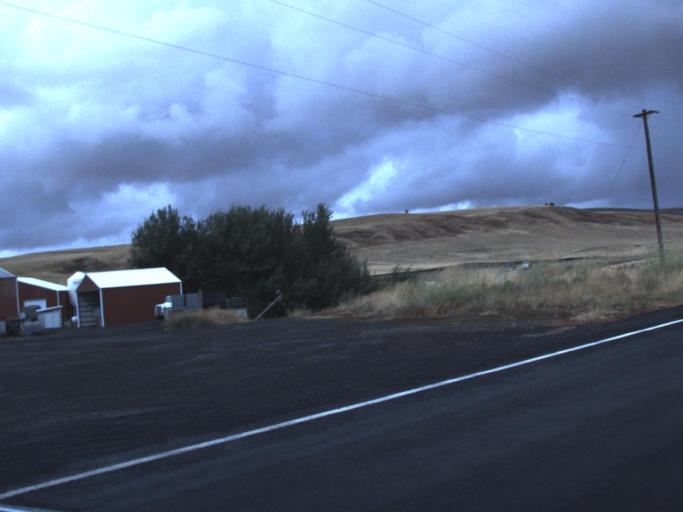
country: US
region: Washington
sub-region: Spokane County
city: Medical Lake
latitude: 47.6900
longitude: -117.8823
